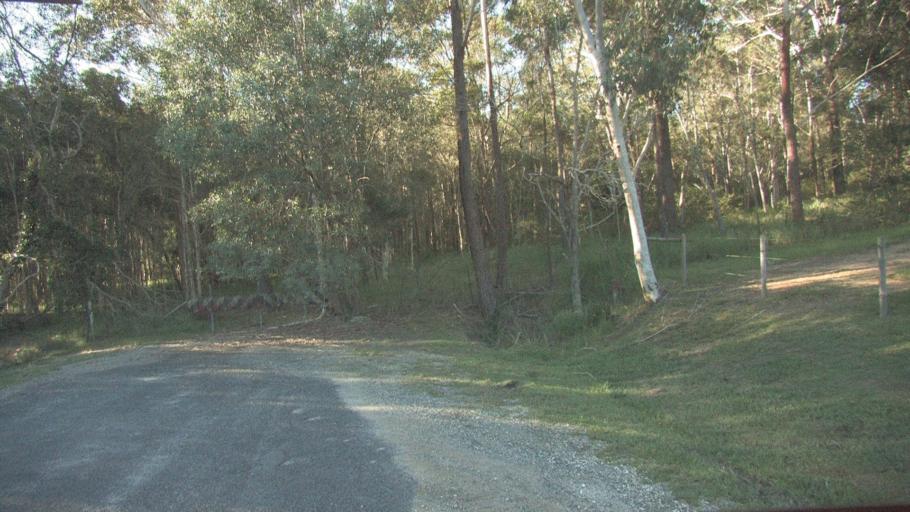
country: AU
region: Queensland
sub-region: Redland
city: Redland Bay
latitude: -27.6568
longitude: 153.2670
